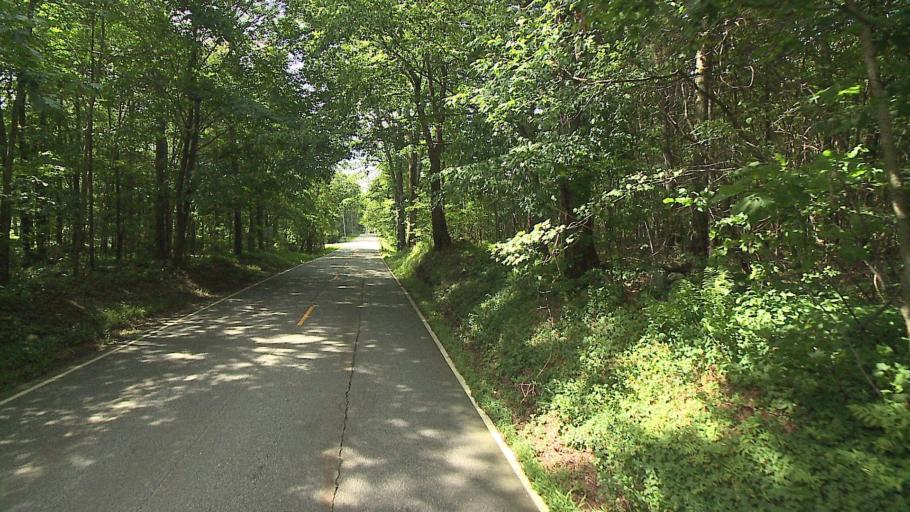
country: US
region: Connecticut
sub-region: Litchfield County
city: Litchfield
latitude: 41.6978
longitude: -73.1931
